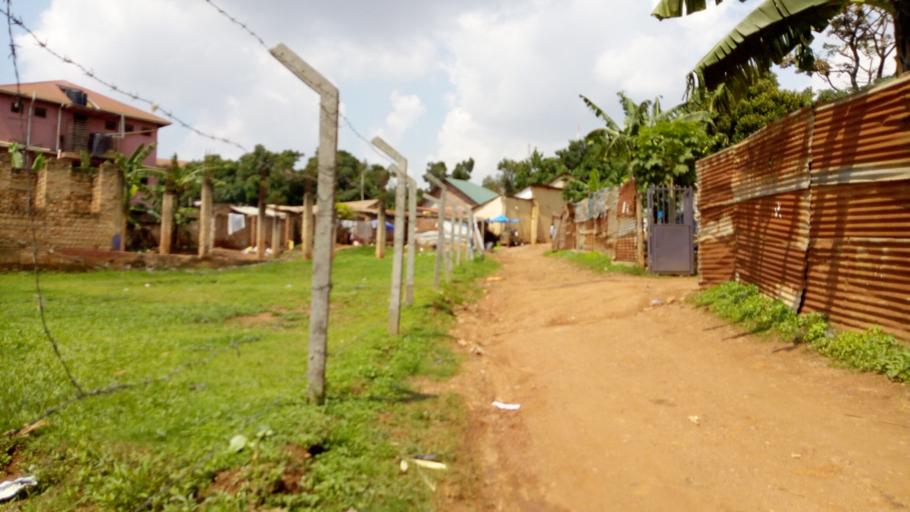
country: UG
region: Central Region
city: Kampala Central Division
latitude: 0.3431
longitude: 32.5657
